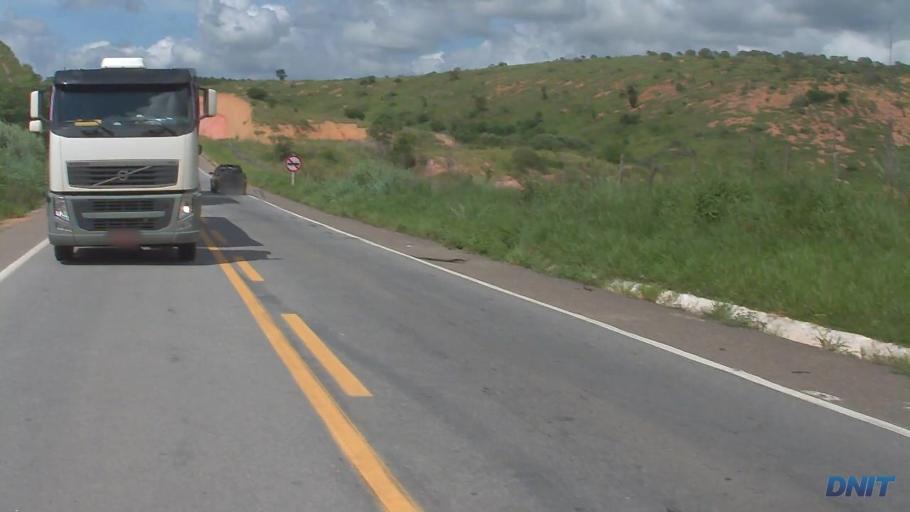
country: BR
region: Minas Gerais
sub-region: Governador Valadares
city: Governador Valadares
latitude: -19.0668
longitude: -42.1666
